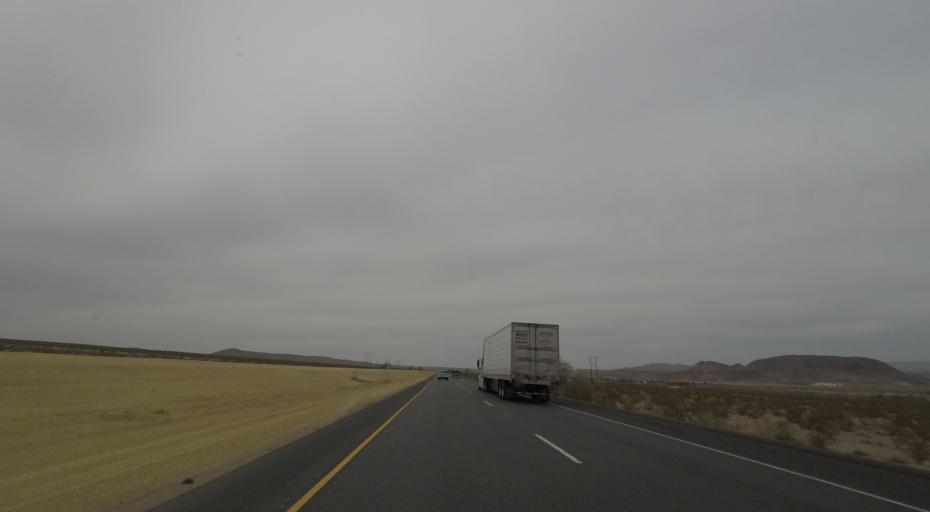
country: US
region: California
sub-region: San Bernardino County
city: Barstow
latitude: 34.8491
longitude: -116.8606
